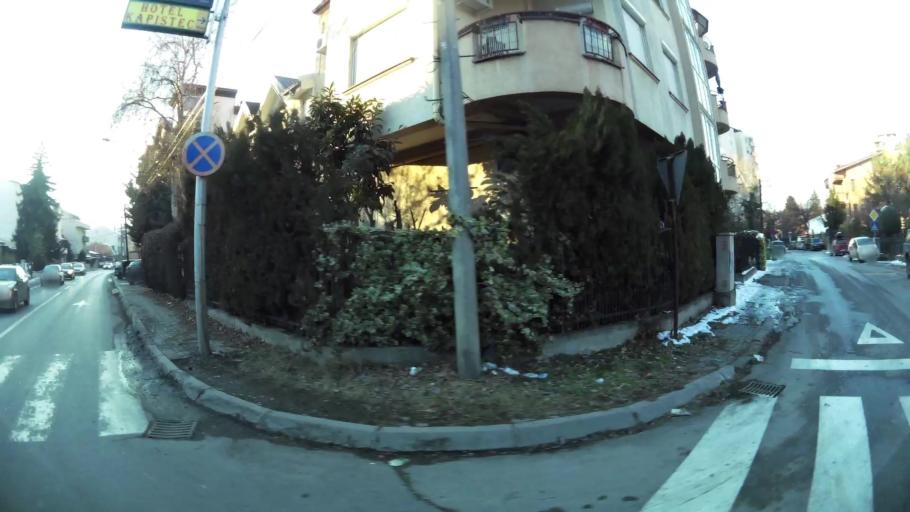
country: MK
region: Karpos
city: Skopje
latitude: 41.9934
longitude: 21.4078
